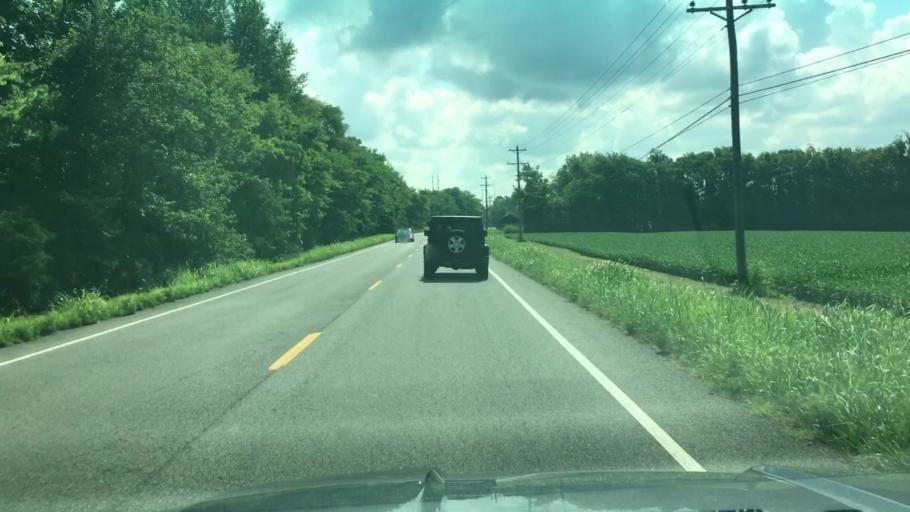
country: US
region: Tennessee
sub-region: Williamson County
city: Nolensville
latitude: 35.8679
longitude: -86.7040
